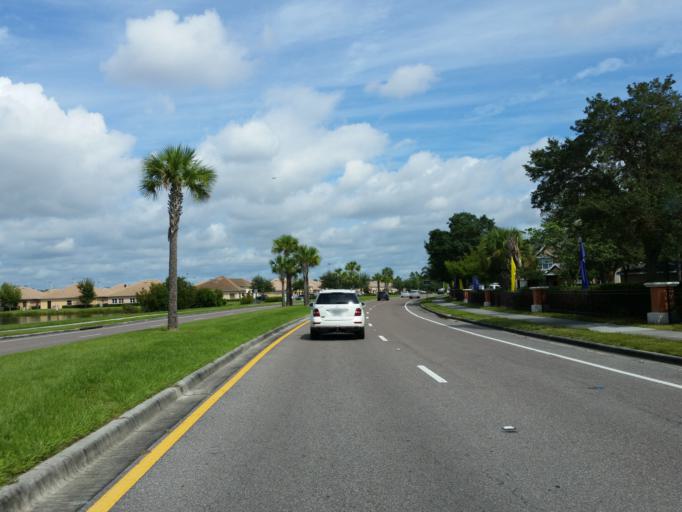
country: US
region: Florida
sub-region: Hillsborough County
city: Brandon
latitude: 27.9168
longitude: -82.3237
